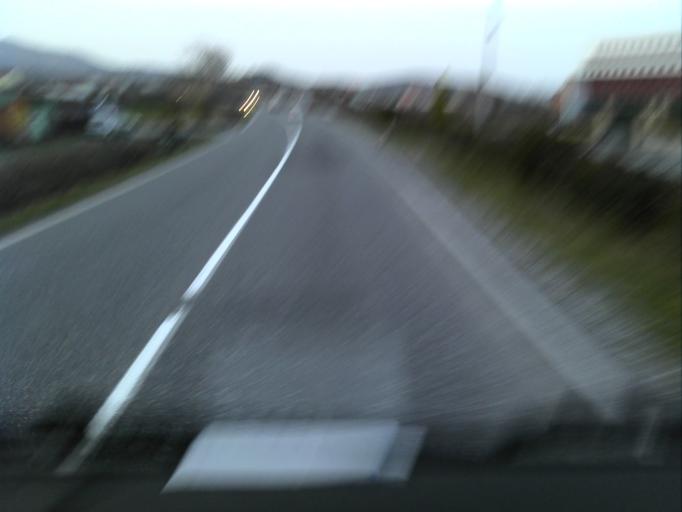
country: AL
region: Shkoder
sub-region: Rrethi i Malesia e Madhe
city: Kuc
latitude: 42.0074
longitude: 19.5220
